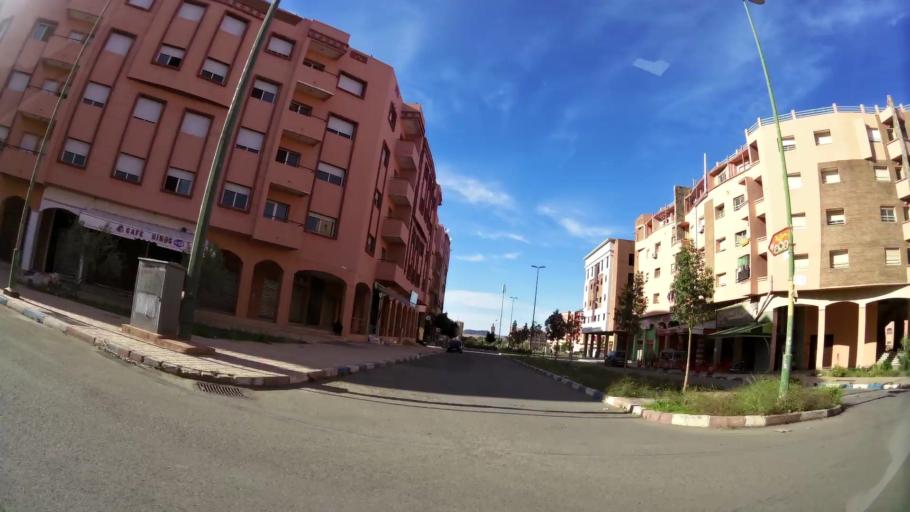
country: MA
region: Marrakech-Tensift-Al Haouz
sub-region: Marrakech
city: Marrakesh
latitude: 31.6847
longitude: -8.0694
